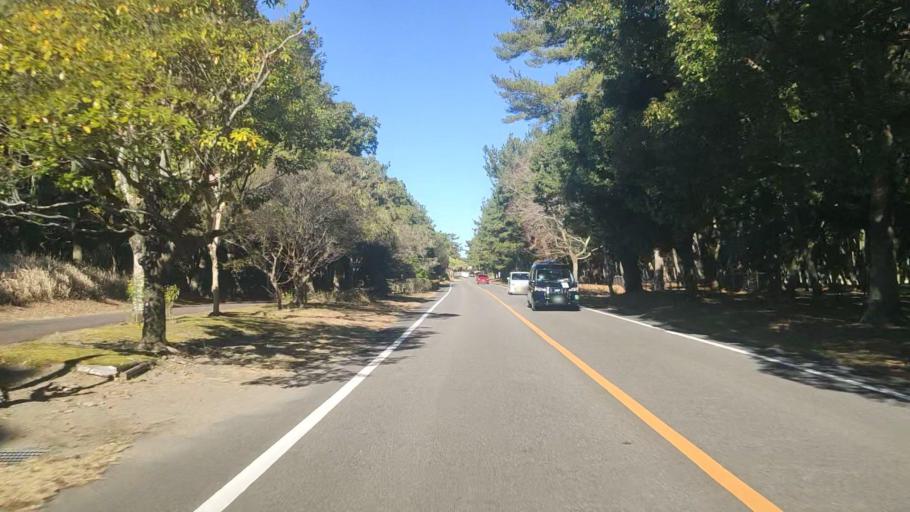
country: JP
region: Miyazaki
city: Miyazaki-shi
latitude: 31.9489
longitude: 131.4658
